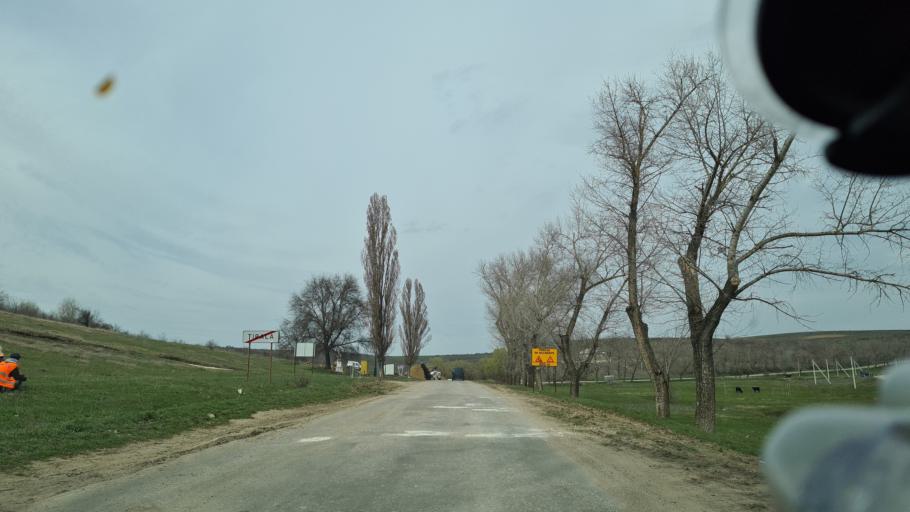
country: MD
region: Chisinau
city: Singera
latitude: 46.8396
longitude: 28.9794
